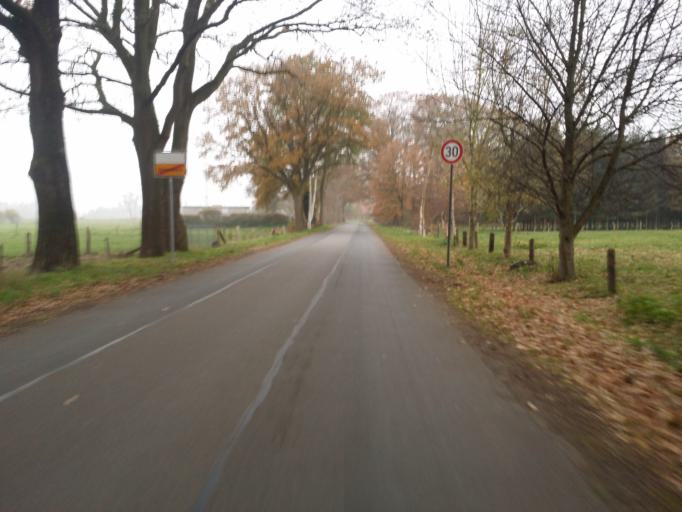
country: DE
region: Lower Saxony
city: Delmenhorst
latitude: 53.0206
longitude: 8.6253
